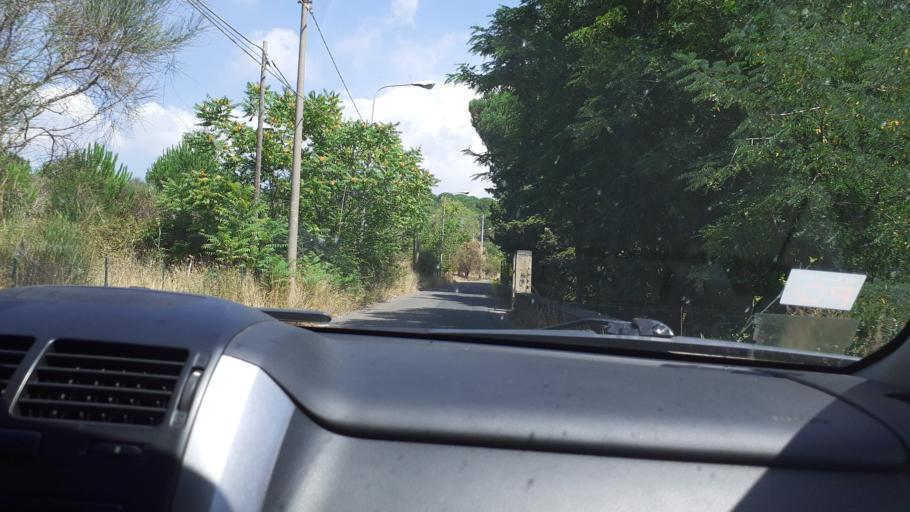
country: IT
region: Sicily
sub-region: Catania
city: Nicolosi
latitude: 37.6261
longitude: 15.0246
